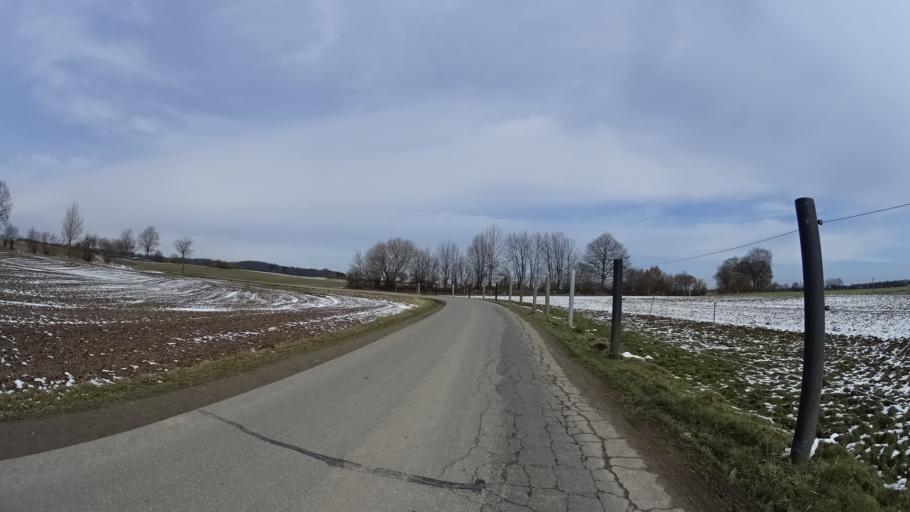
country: DE
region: Schleswig-Holstein
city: Rendswuhren
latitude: 54.0912
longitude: 10.1992
